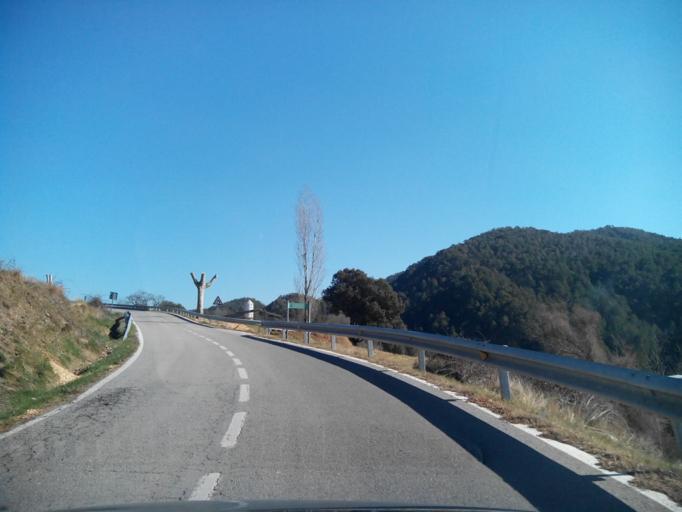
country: ES
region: Catalonia
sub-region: Provincia de Barcelona
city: Borreda
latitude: 42.1298
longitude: 1.9914
